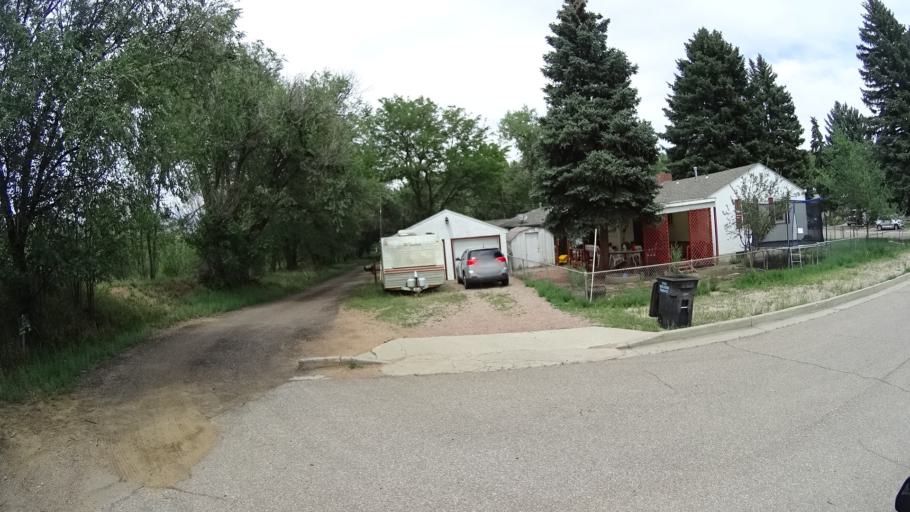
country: US
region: Colorado
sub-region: El Paso County
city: Colorado Springs
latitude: 38.8557
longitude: -104.8381
